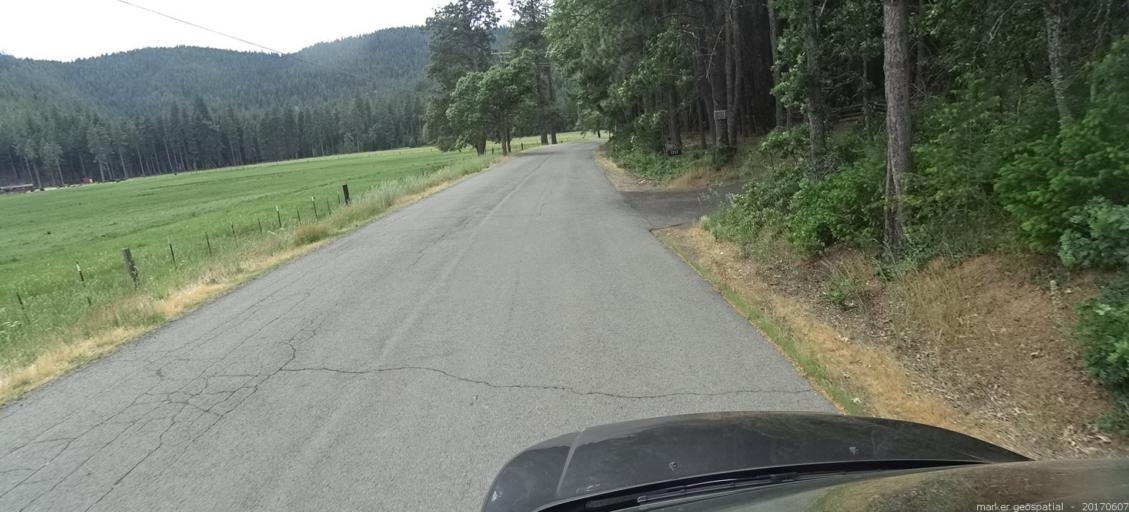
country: US
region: California
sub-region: Siskiyou County
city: Mount Shasta
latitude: 41.3249
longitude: -122.3542
